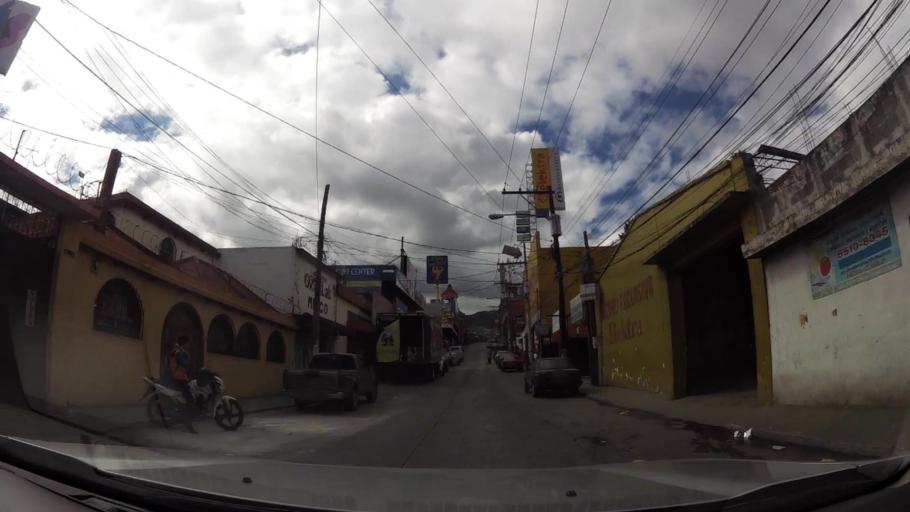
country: GT
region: Guatemala
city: Mixco
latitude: 14.6297
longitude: -90.6046
